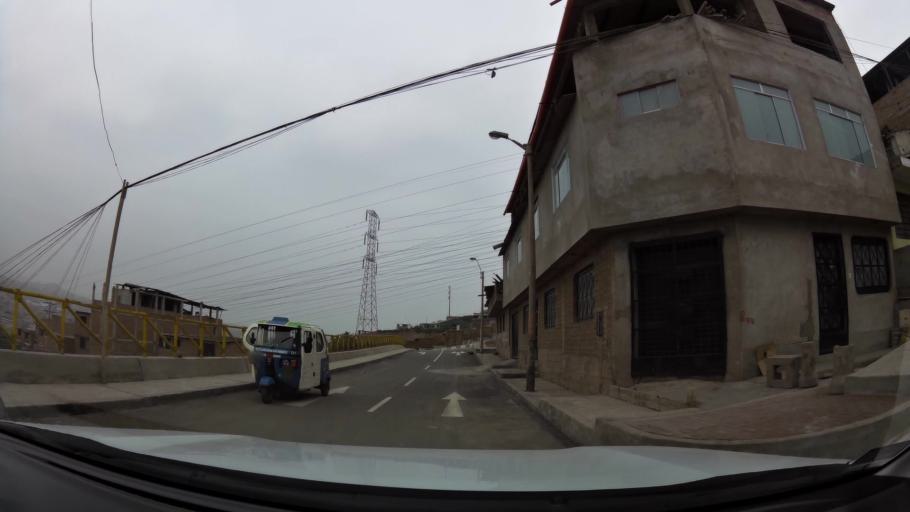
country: PE
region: Lima
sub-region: Lima
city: Surco
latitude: -12.1820
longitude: -76.9505
